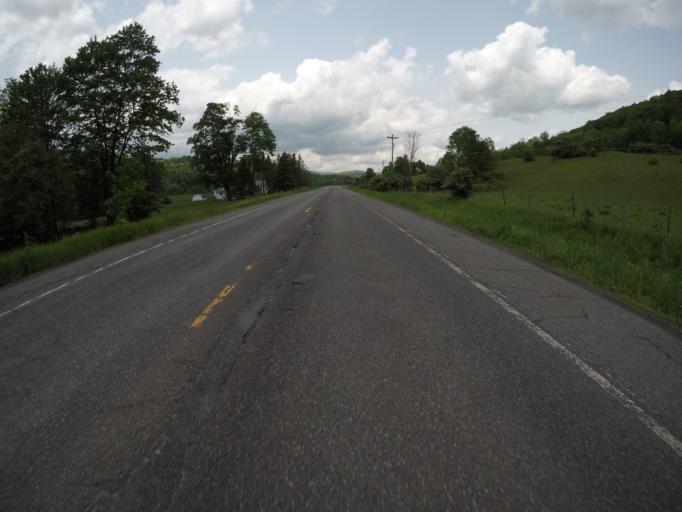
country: US
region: New York
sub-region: Delaware County
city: Stamford
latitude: 42.2353
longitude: -74.5986
